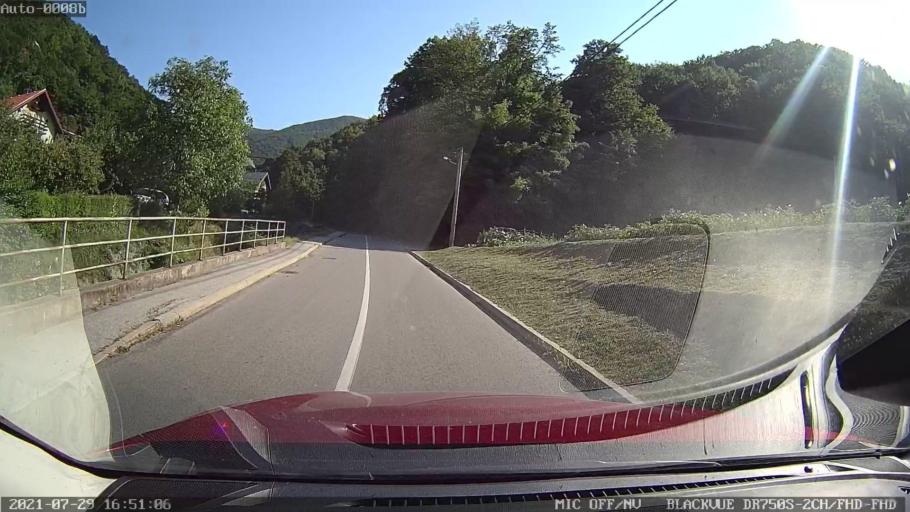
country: HR
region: Varazdinska
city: Ivanec
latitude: 46.2091
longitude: 16.1320
